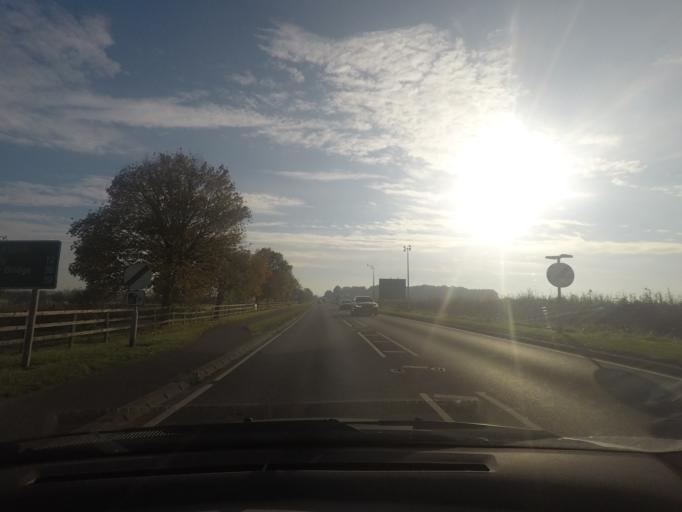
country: GB
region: England
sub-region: East Riding of Yorkshire
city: Londesborough
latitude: 53.8731
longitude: -0.6978
